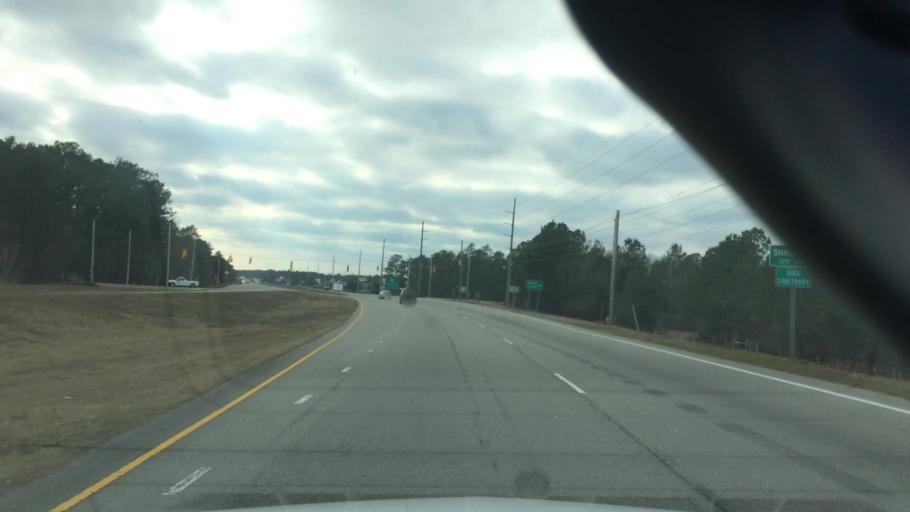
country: US
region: North Carolina
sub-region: Brunswick County
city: Shallotte
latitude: 33.9885
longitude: -78.3887
